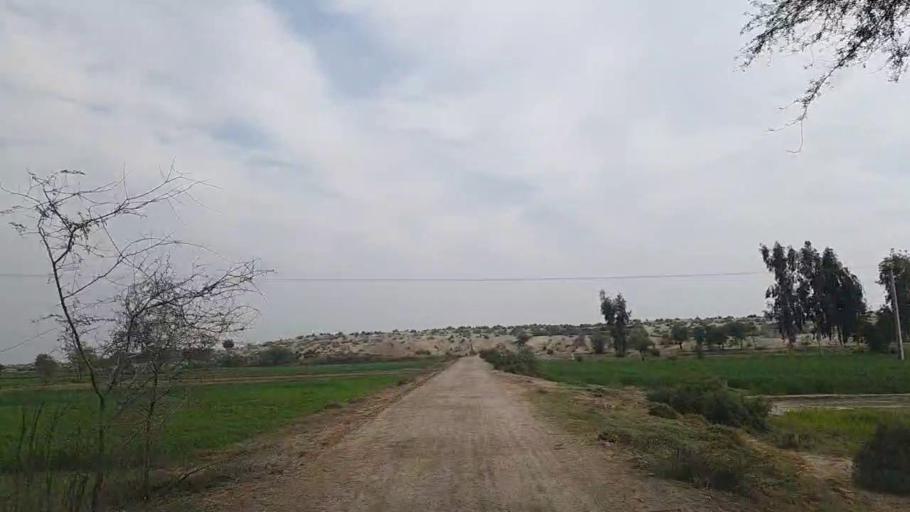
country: PK
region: Sindh
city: Daur
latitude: 26.4334
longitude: 68.4703
